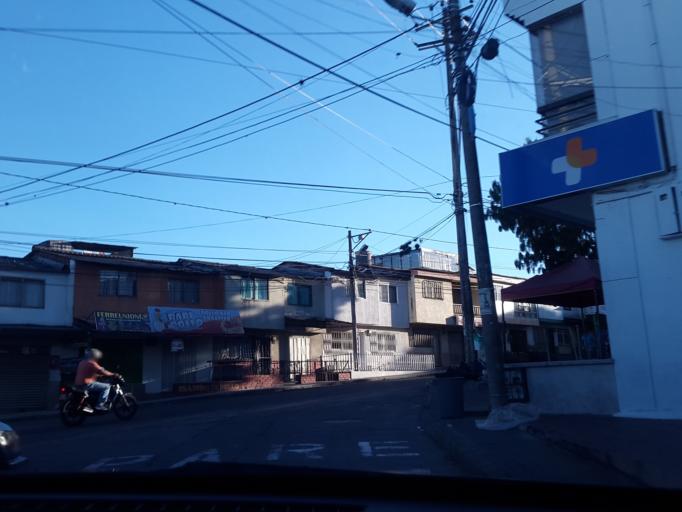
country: CO
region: Quindio
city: Armenia
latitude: 4.5342
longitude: -75.6887
